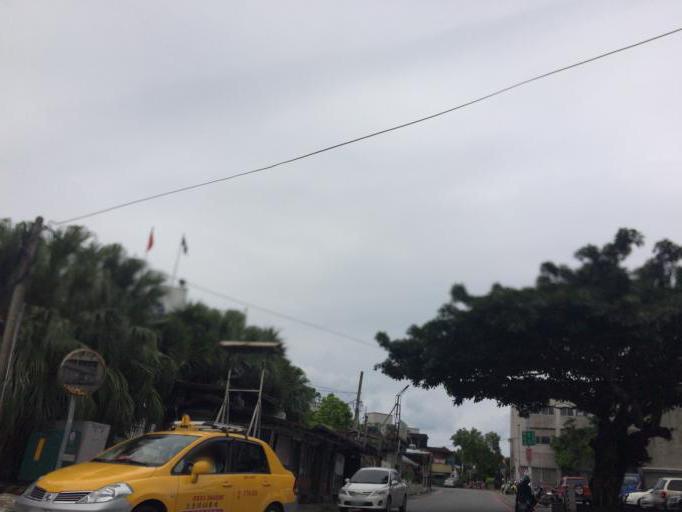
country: TW
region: Taiwan
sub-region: Hualien
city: Hualian
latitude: 23.9784
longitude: 121.6132
